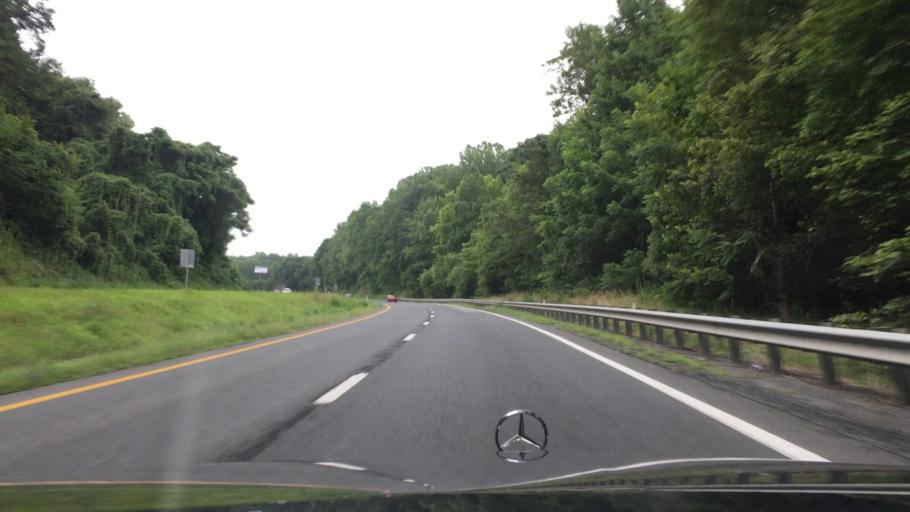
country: US
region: Virginia
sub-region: Campbell County
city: Concord
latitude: 37.3752
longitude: -79.0403
